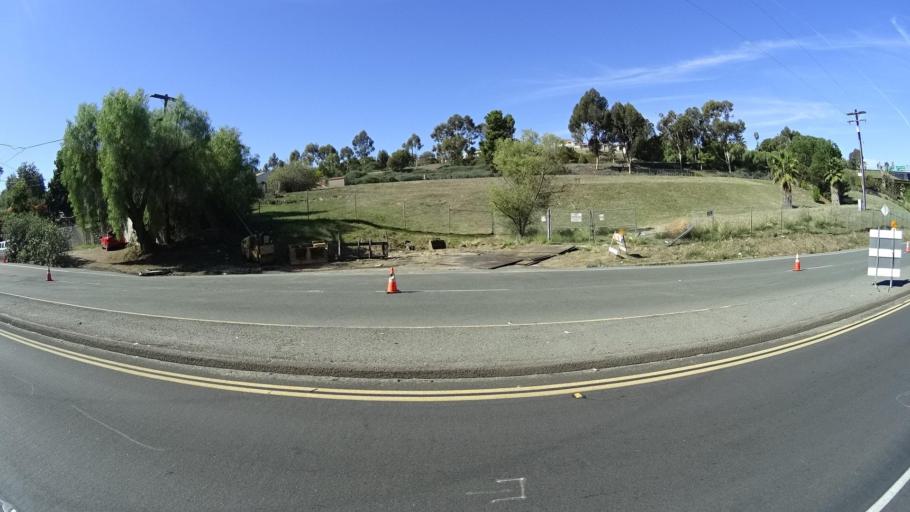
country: US
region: California
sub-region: San Diego County
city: Spring Valley
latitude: 32.7410
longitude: -117.0145
